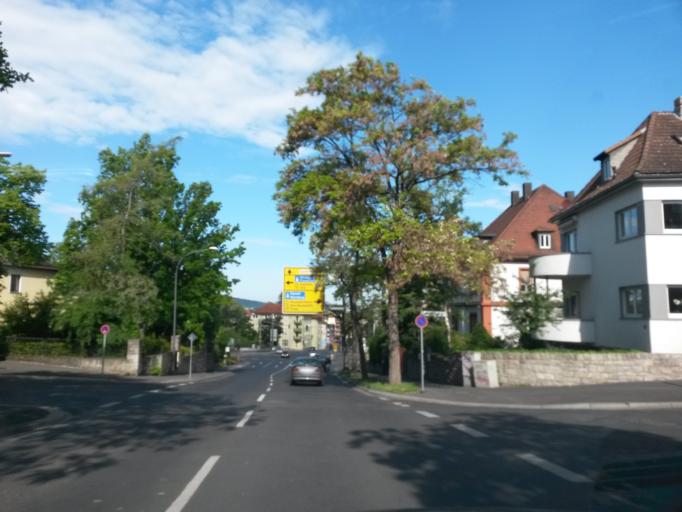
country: DE
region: Bavaria
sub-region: Regierungsbezirk Unterfranken
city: Wuerzburg
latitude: 49.7916
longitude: 9.9505
